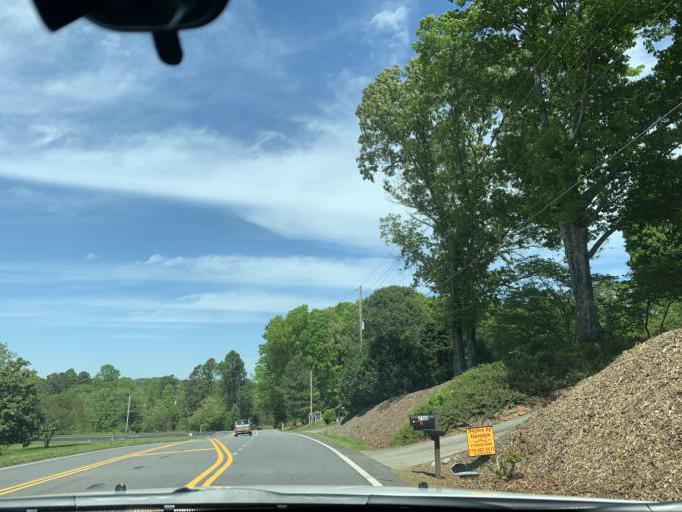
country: US
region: Georgia
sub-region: Hall County
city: Flowery Branch
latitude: 34.2548
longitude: -84.0246
